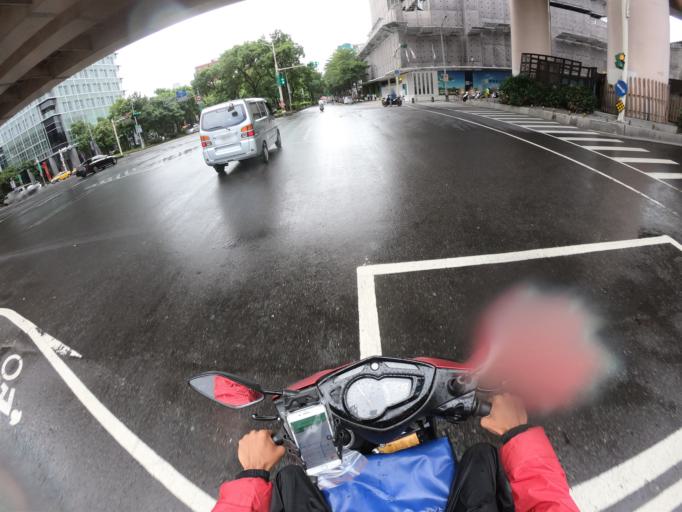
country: TW
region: Taipei
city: Taipei
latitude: 25.0452
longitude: 121.5487
